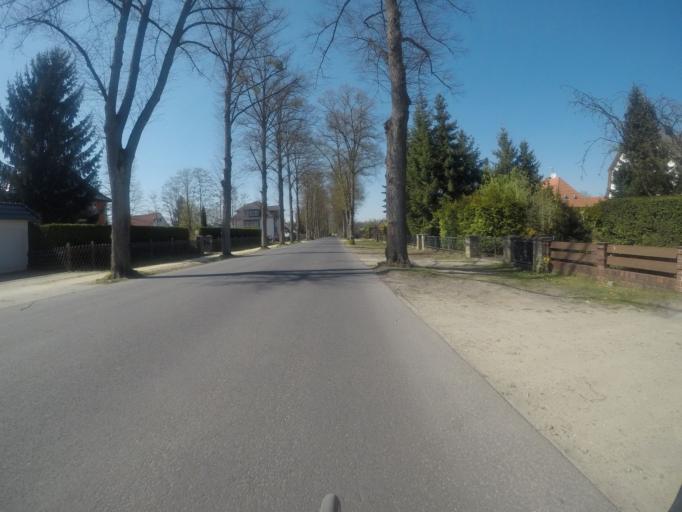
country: DE
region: Brandenburg
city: Wandlitz
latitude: 52.7471
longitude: 13.4624
